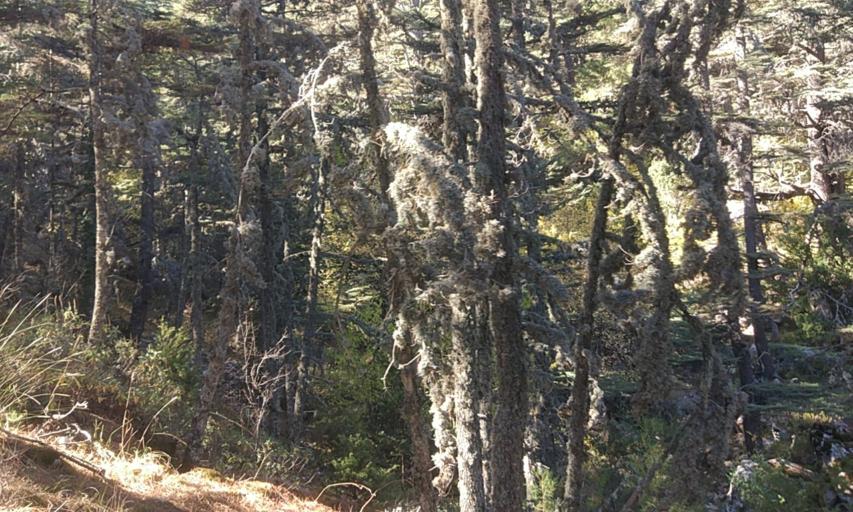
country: TR
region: Antalya
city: Altinyaka
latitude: 36.5619
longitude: 30.4165
